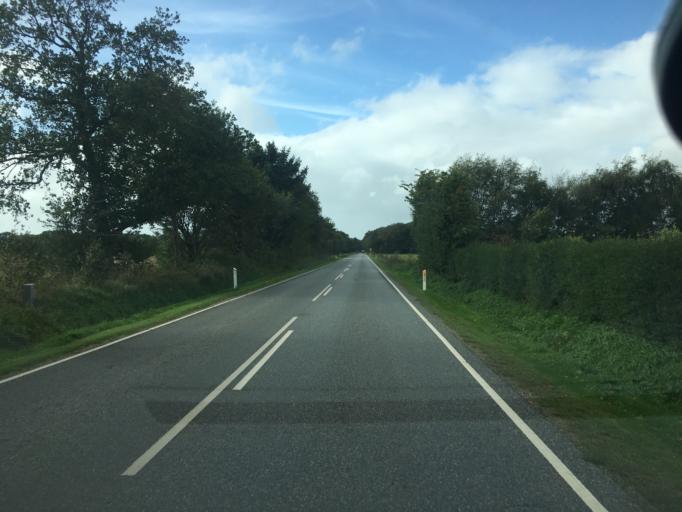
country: DK
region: South Denmark
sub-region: Tonder Kommune
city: Tonder
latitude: 55.0086
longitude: 8.8157
